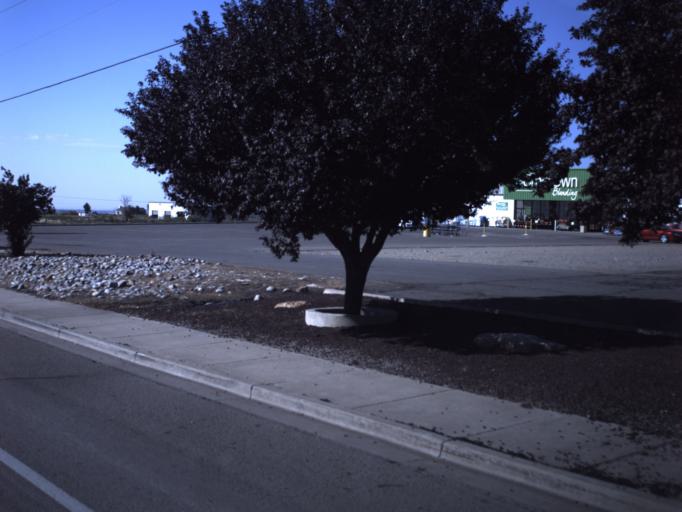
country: US
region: Utah
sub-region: San Juan County
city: Blanding
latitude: 37.6130
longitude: -109.4790
